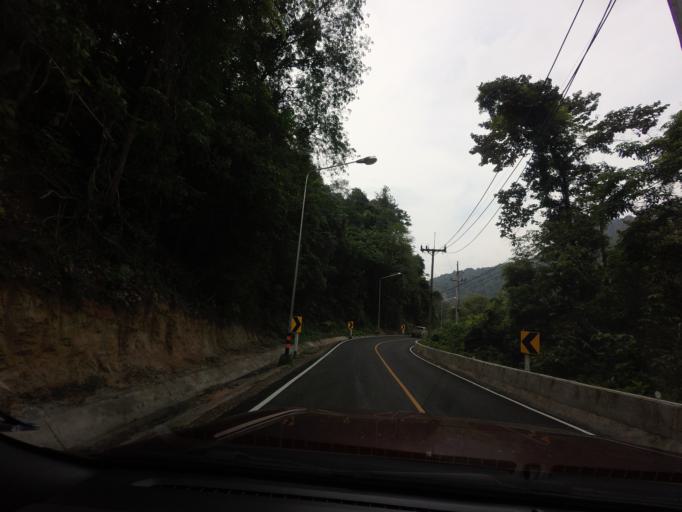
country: TH
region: Yala
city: Than To
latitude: 6.1340
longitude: 101.2975
